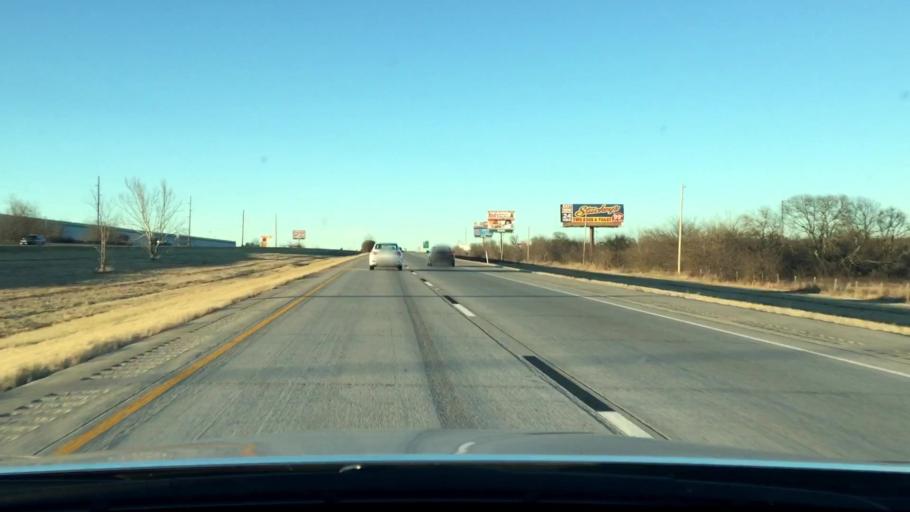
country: US
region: Oklahoma
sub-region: Love County
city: Marietta
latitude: 33.9303
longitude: -97.1346
